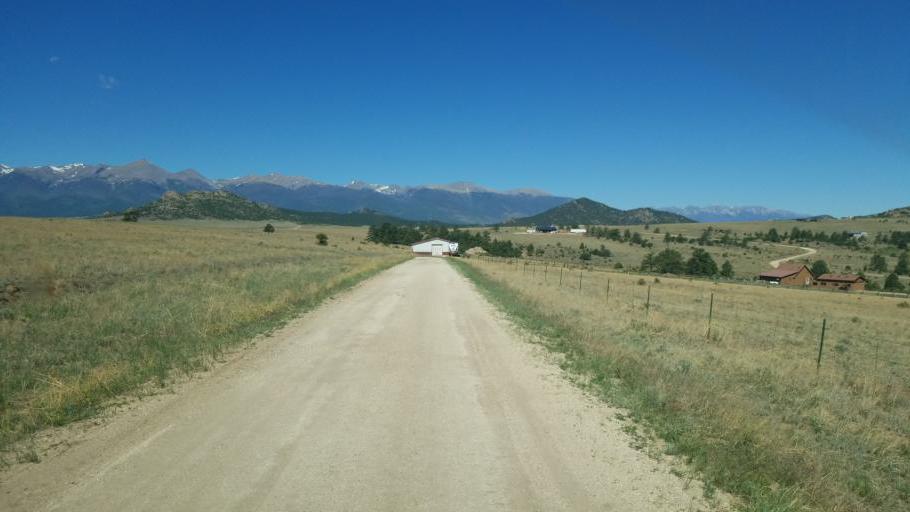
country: US
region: Colorado
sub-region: Custer County
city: Westcliffe
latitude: 38.2341
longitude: -105.4737
